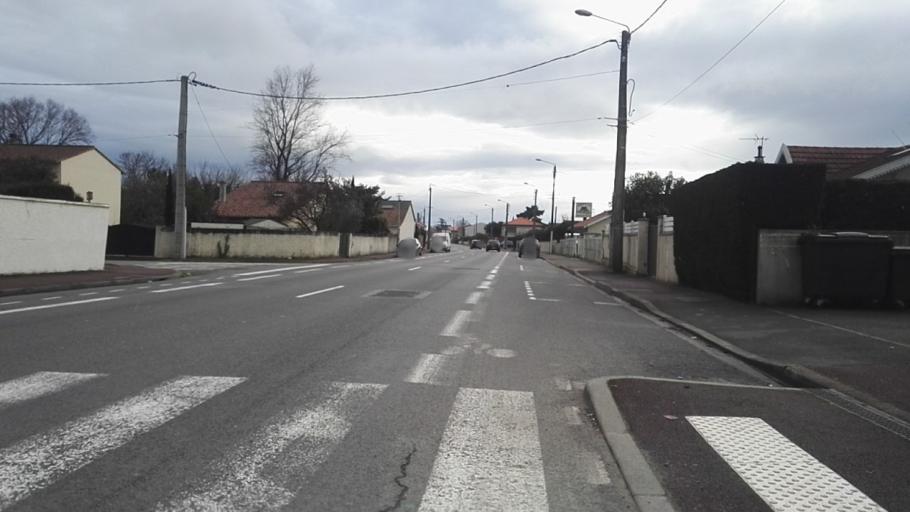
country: FR
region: Aquitaine
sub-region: Departement de la Gironde
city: Eysines
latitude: 44.8601
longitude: -0.6429
